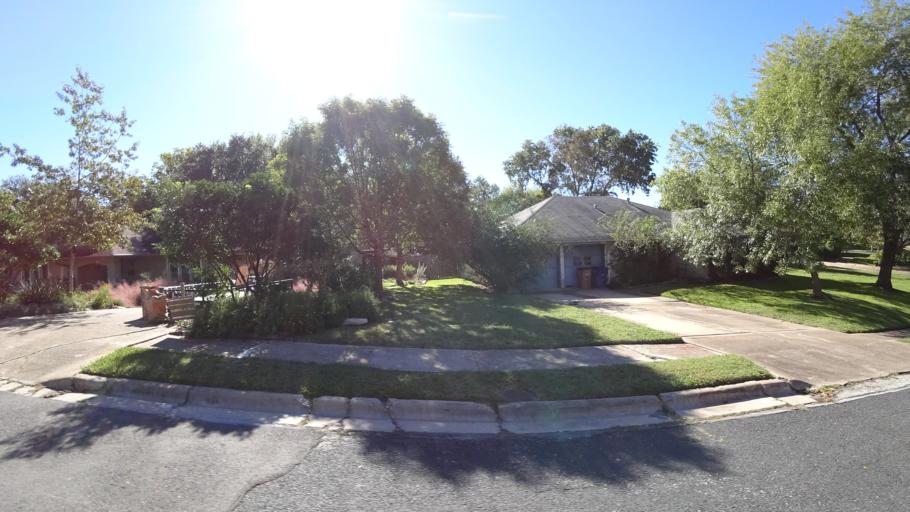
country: US
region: Texas
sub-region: Travis County
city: Rollingwood
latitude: 30.2188
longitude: -97.8108
